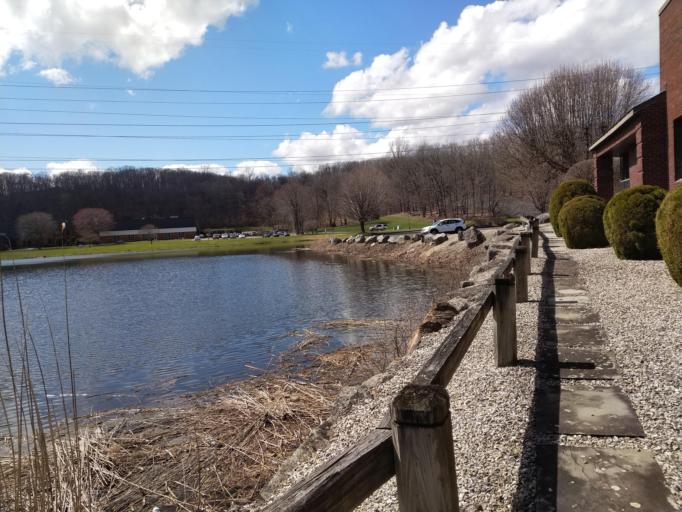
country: US
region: Connecticut
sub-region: Fairfield County
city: Bethel
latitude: 41.4241
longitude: -73.4006
